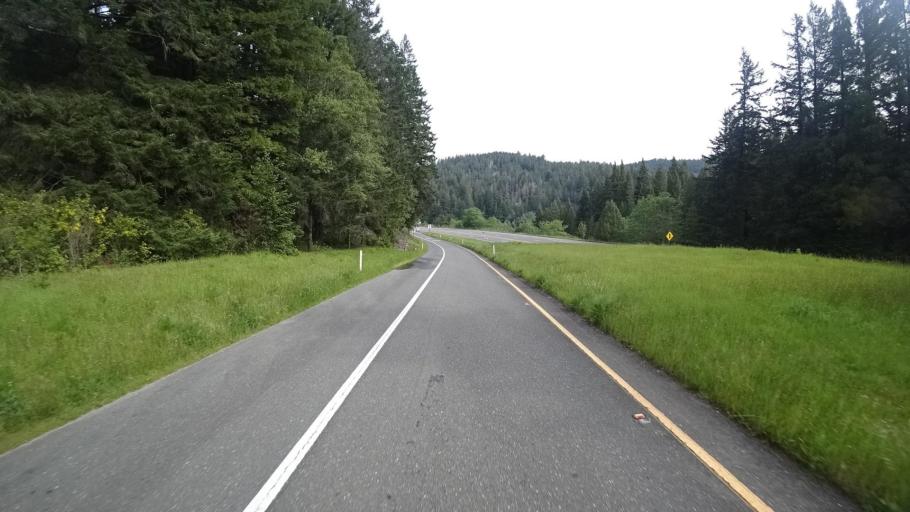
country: US
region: California
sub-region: Humboldt County
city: Redway
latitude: 40.2516
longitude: -123.8325
